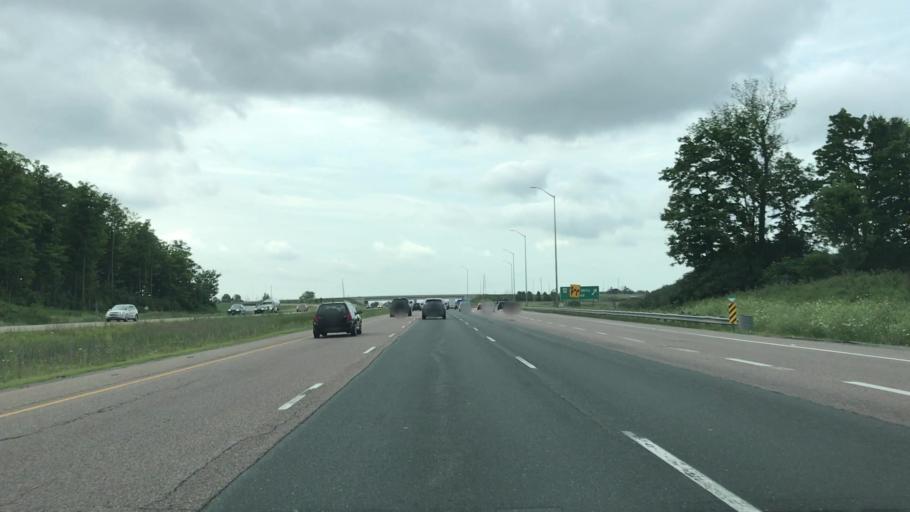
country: CA
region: Ontario
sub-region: York
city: Richmond Hill
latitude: 43.9074
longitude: -79.3859
